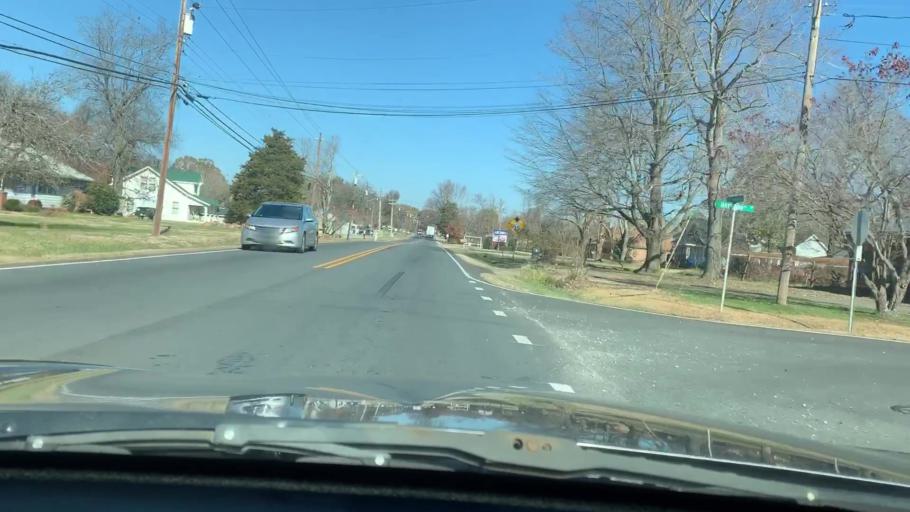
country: US
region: North Carolina
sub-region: Alamance County
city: Haw River
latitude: 36.0852
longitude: -79.3480
